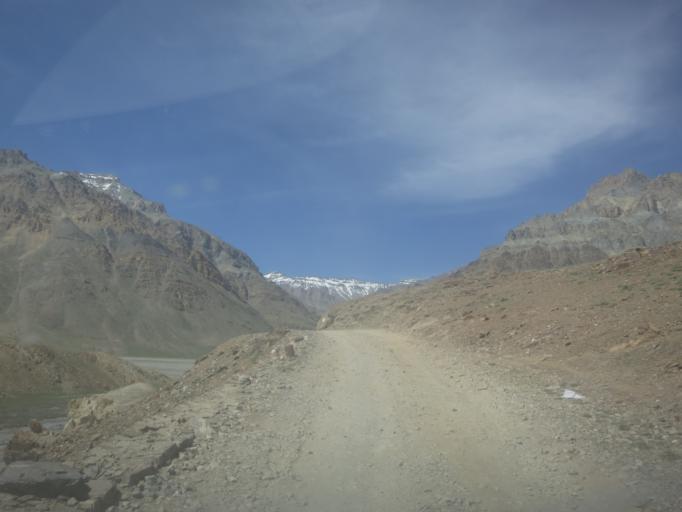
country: IN
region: Himachal Pradesh
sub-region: Kulu
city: Manali
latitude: 32.4504
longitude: 77.6959
